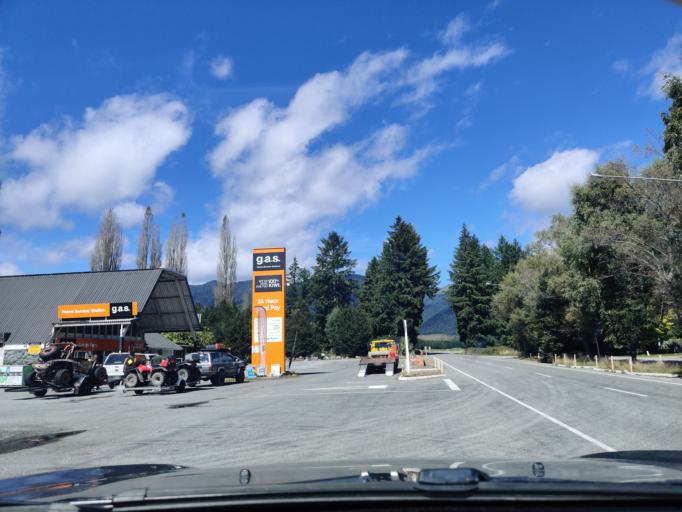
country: NZ
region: West Coast
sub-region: Buller District
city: Westport
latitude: -42.3352
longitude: 172.1826
